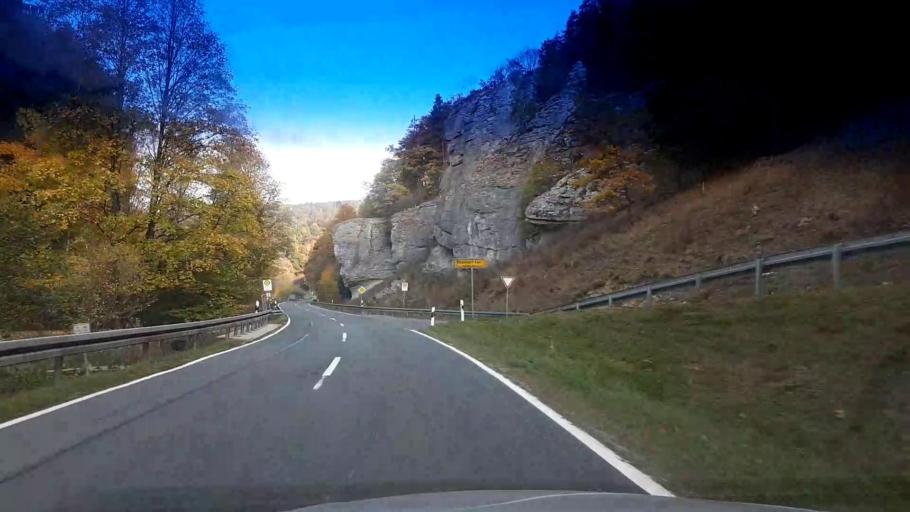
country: DE
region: Bavaria
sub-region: Upper Franconia
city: Weismain
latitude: 50.0476
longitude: 11.2302
